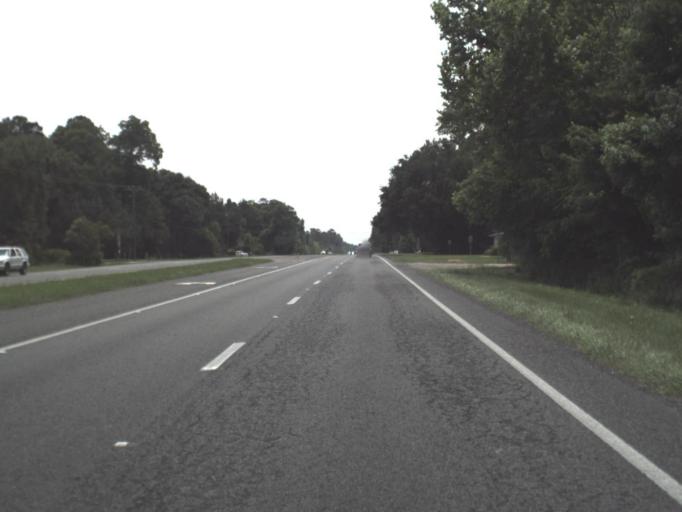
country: US
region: Florida
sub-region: Nassau County
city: Nassau Village-Ratliff
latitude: 30.5328
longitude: -81.8077
